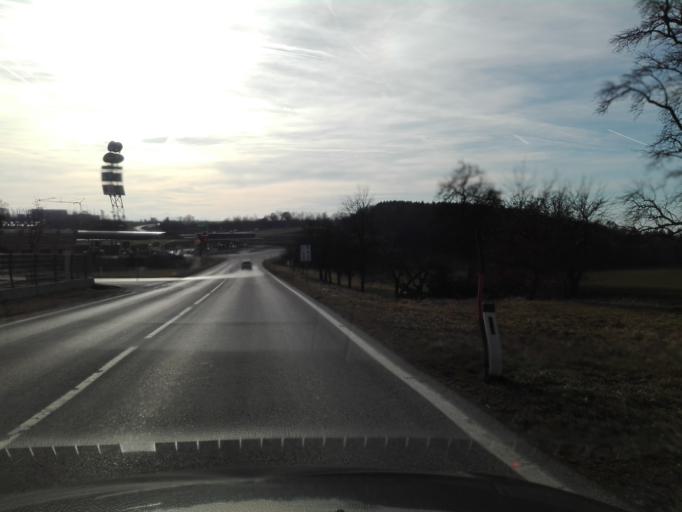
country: AT
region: Lower Austria
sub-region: Politischer Bezirk Amstetten
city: Zeillern
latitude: 48.1185
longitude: 14.7327
